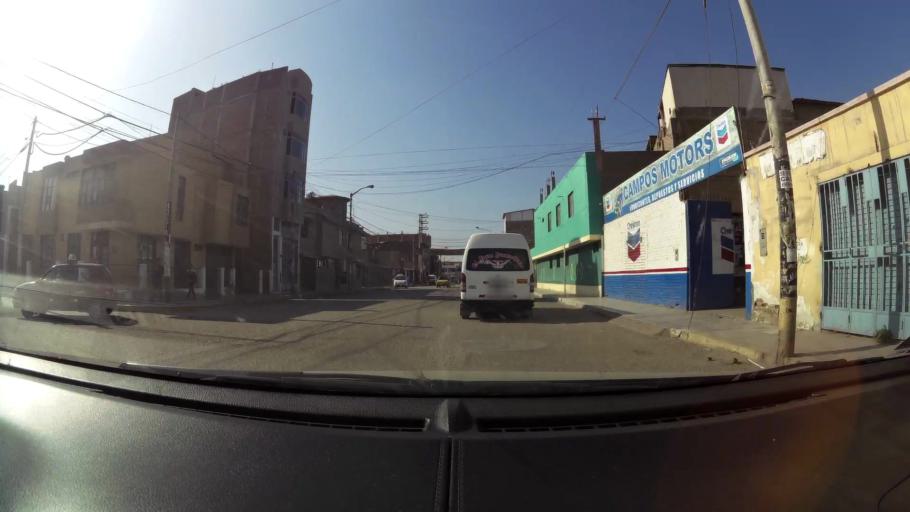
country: PE
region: Lambayeque
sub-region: Provincia de Chiclayo
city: Chiclayo
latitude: -6.7641
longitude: -79.8443
